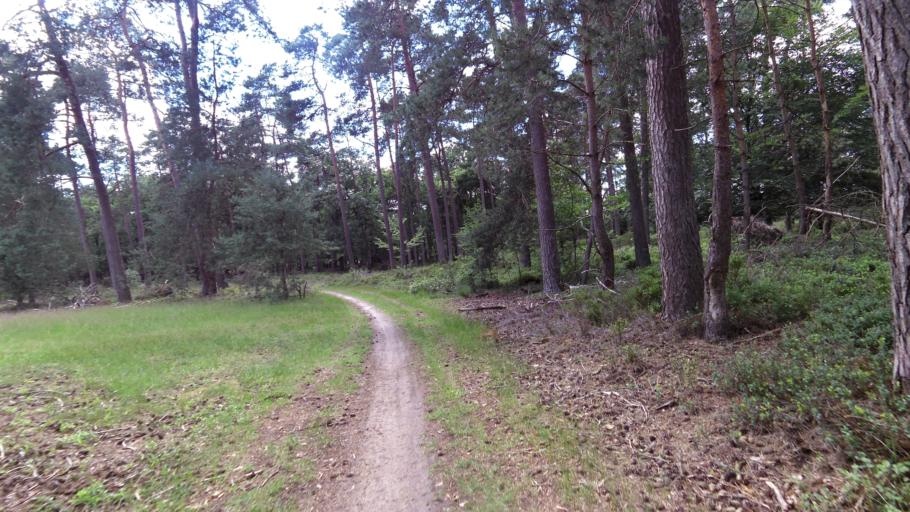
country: NL
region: Gelderland
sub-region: Gemeente Epe
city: Vaassen
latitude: 52.2561
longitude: 5.8973
